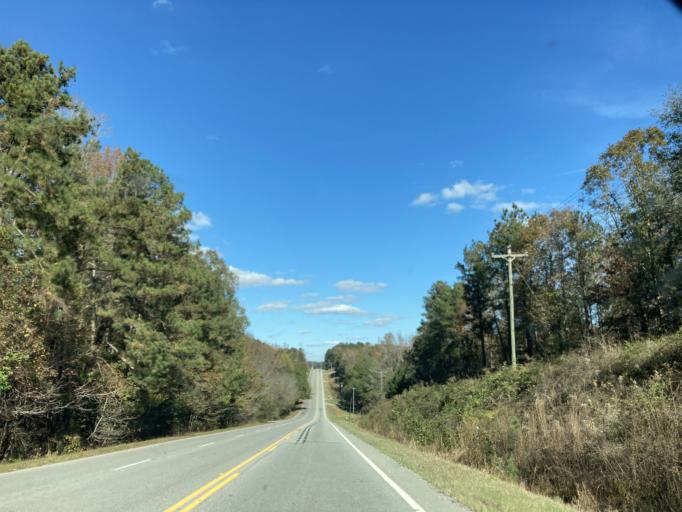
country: US
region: Georgia
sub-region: Jones County
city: Gray
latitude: 32.9066
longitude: -83.5218
